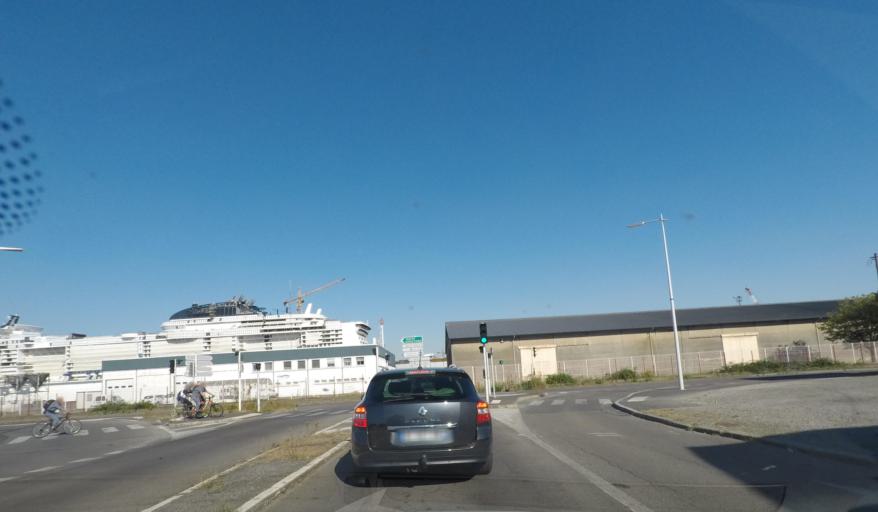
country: FR
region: Pays de la Loire
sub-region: Departement de la Loire-Atlantique
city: Saint-Nazaire
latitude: 47.2843
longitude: -2.2018
